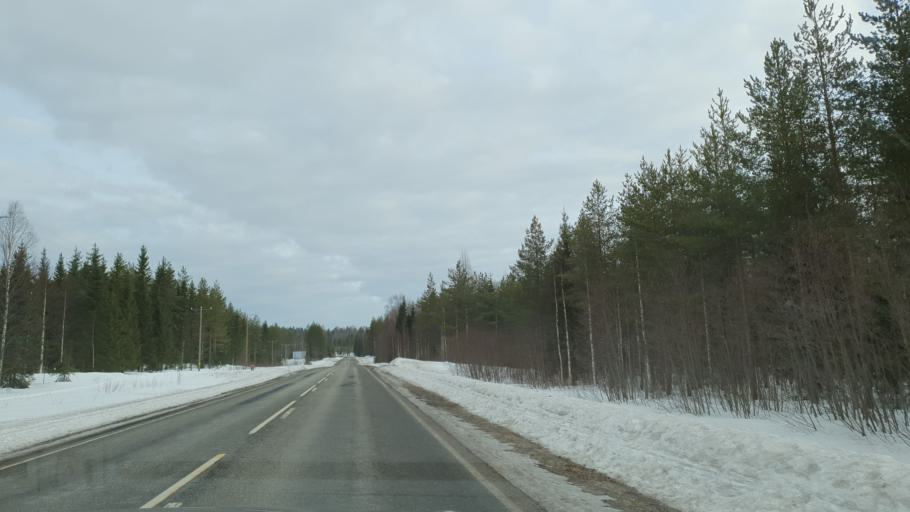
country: FI
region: Kainuu
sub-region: Kajaani
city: Vuokatti
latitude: 64.2381
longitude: 28.0556
